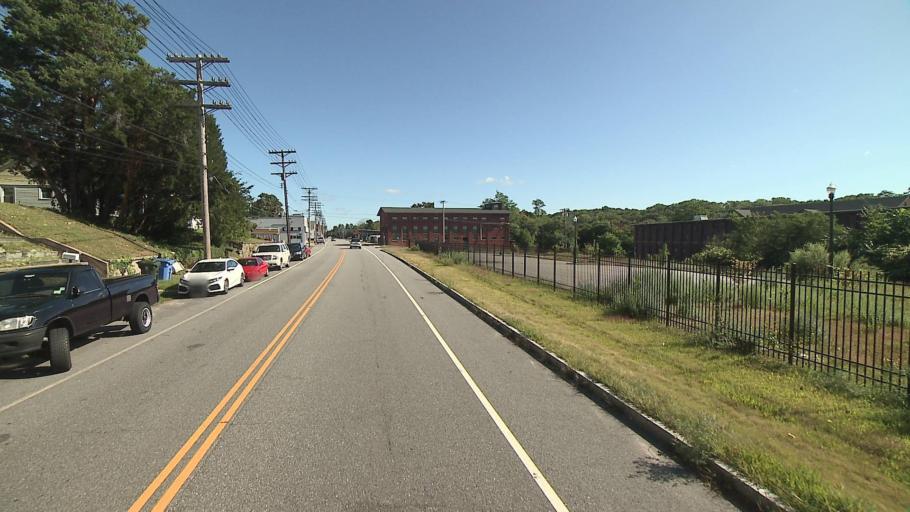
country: US
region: Connecticut
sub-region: New London County
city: Norwich
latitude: 41.5310
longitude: -72.0570
